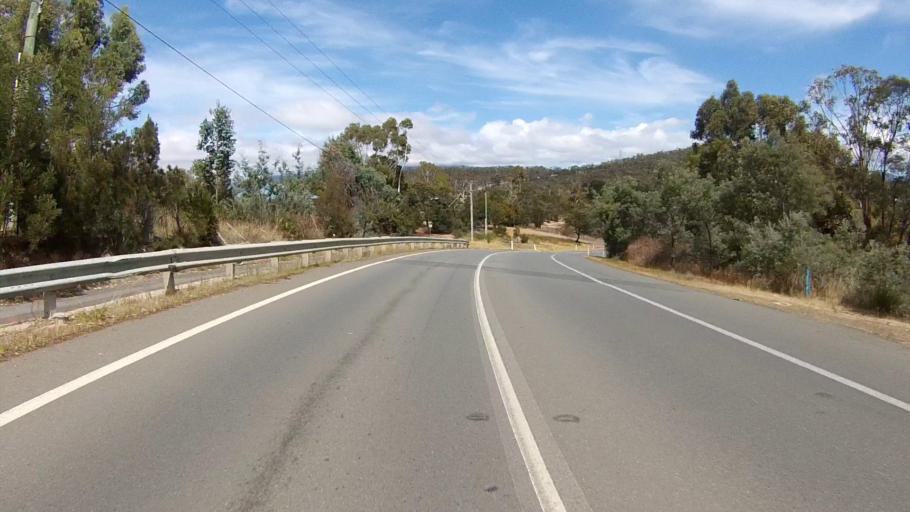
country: AU
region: Tasmania
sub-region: Clarence
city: Lindisfarne
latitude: -42.8235
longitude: 147.3489
